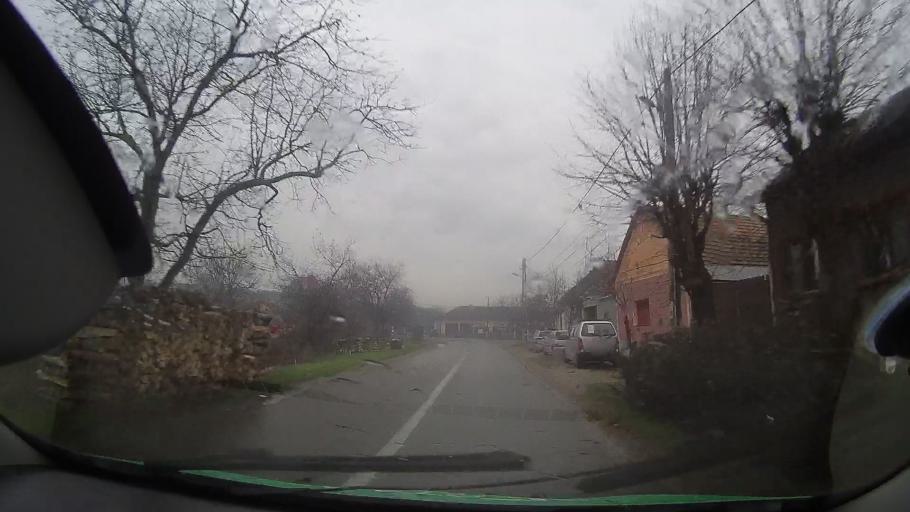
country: RO
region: Bihor
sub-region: Comuna Uileacu de Beius
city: Uileacu de Beius
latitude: 46.6801
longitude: 22.2253
